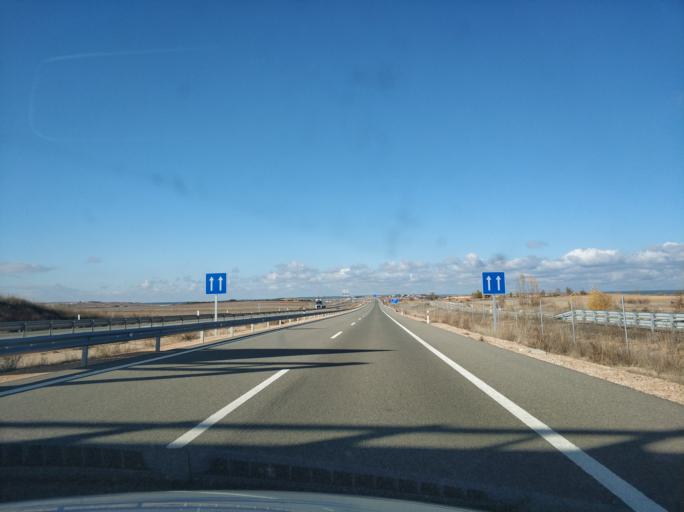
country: ES
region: Castille and Leon
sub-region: Provincia de Soria
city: Frechilla de Almazan
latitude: 41.4515
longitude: -2.5108
